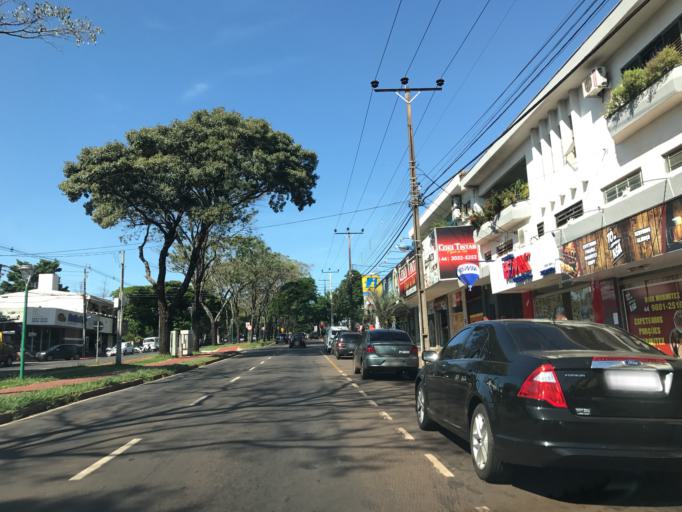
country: BR
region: Parana
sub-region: Maringa
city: Maringa
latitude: -23.4070
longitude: -51.9565
